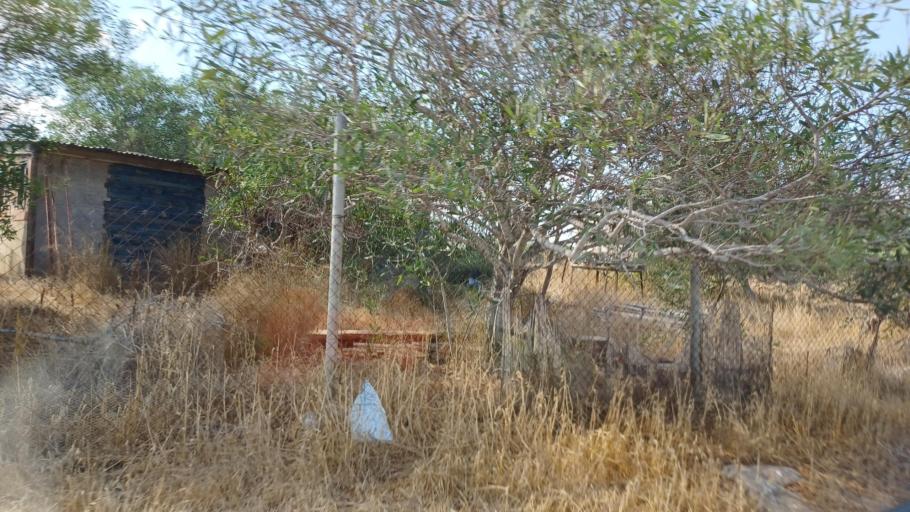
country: CY
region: Ammochostos
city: Deryneia
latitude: 35.0675
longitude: 33.9695
